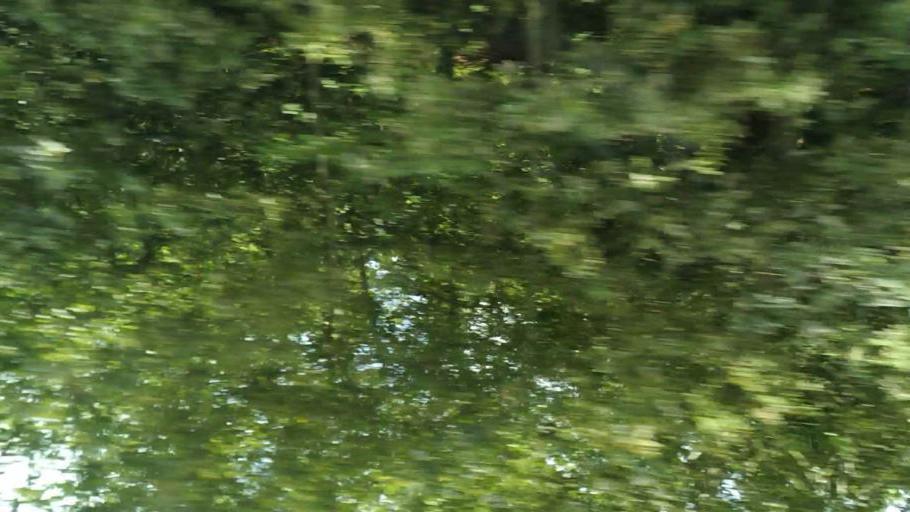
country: DK
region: Central Jutland
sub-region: Syddjurs Kommune
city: Ryomgard
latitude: 56.4590
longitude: 10.5395
